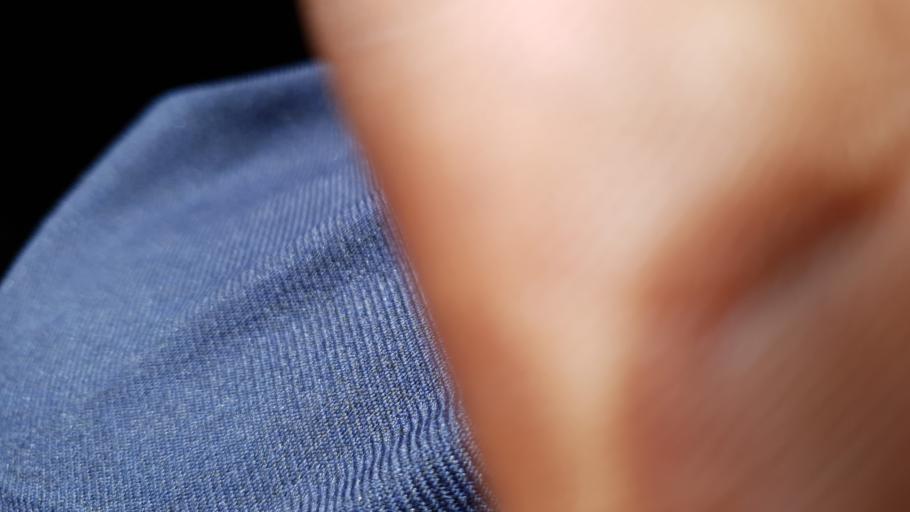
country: ML
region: Koulikoro
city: Kolokani
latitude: 13.3221
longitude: -8.2740
